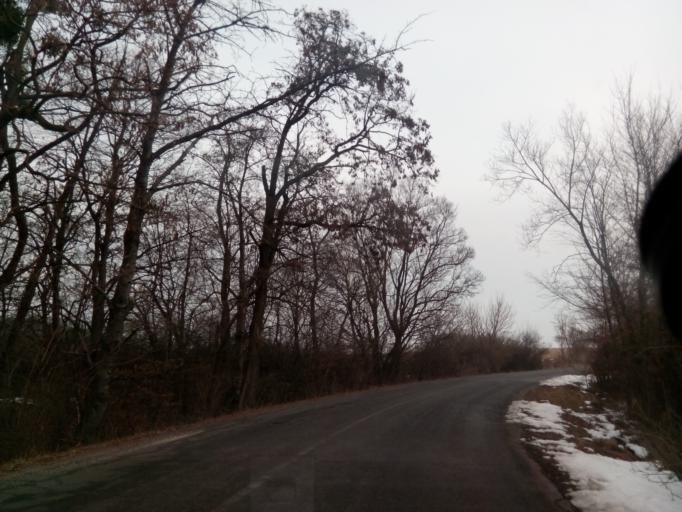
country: HU
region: Borsod-Abauj-Zemplen
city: Gonc
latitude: 48.4869
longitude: 21.3853
